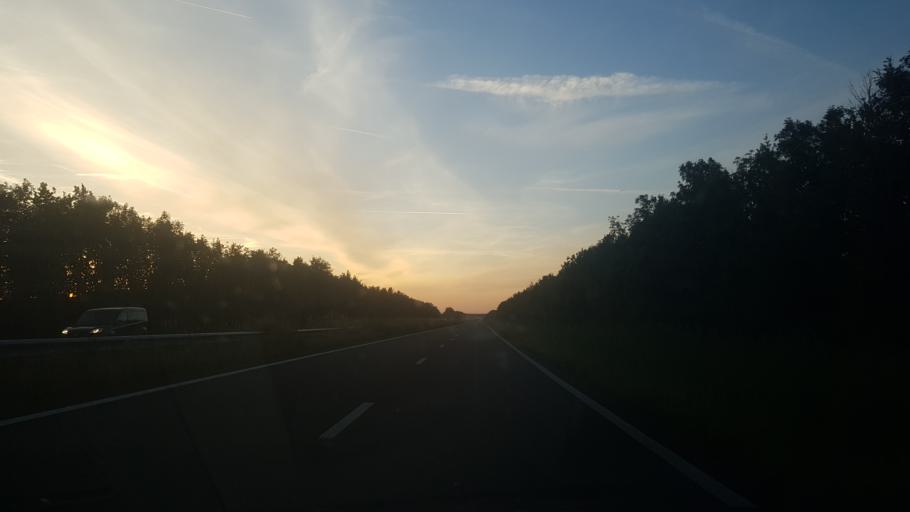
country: NL
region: Flevoland
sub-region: Gemeente Noordoostpolder
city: Ens
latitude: 52.6629
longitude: 5.7947
